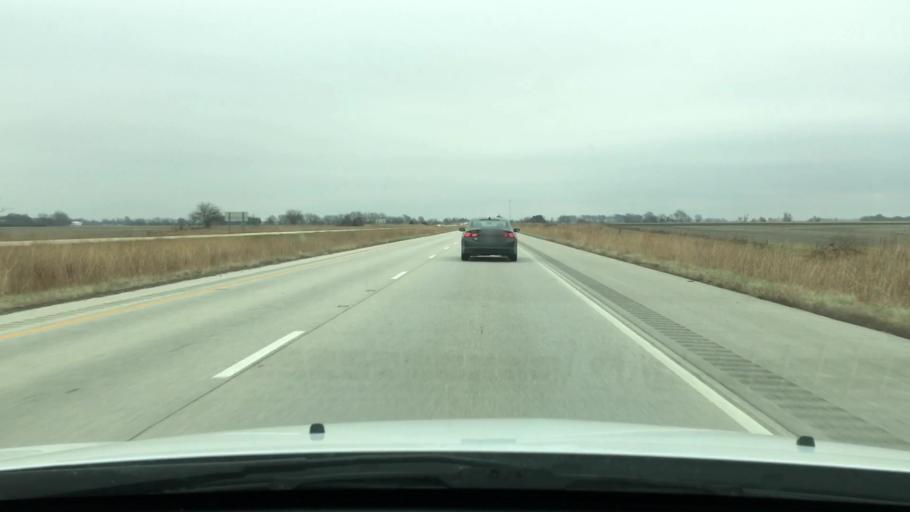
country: US
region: Illinois
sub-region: Sangamon County
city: New Berlin
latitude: 39.7403
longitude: -89.8990
